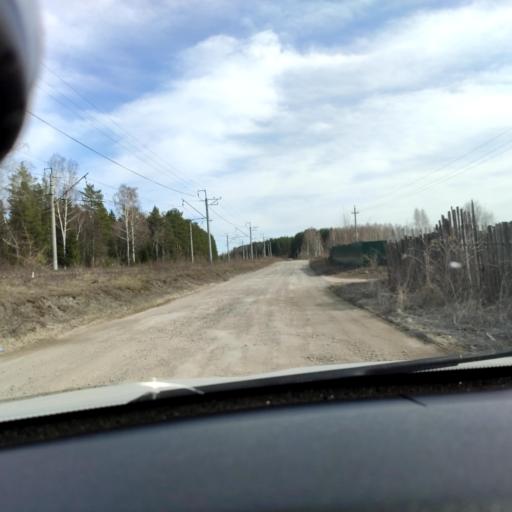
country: RU
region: Perm
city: Overyata
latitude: 58.0587
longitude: 55.9906
